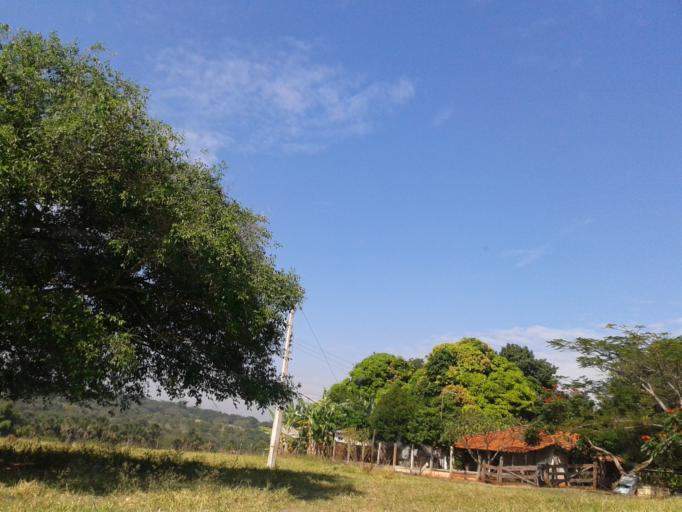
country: BR
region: Minas Gerais
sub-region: Campina Verde
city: Campina Verde
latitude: -19.3920
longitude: -49.6345
